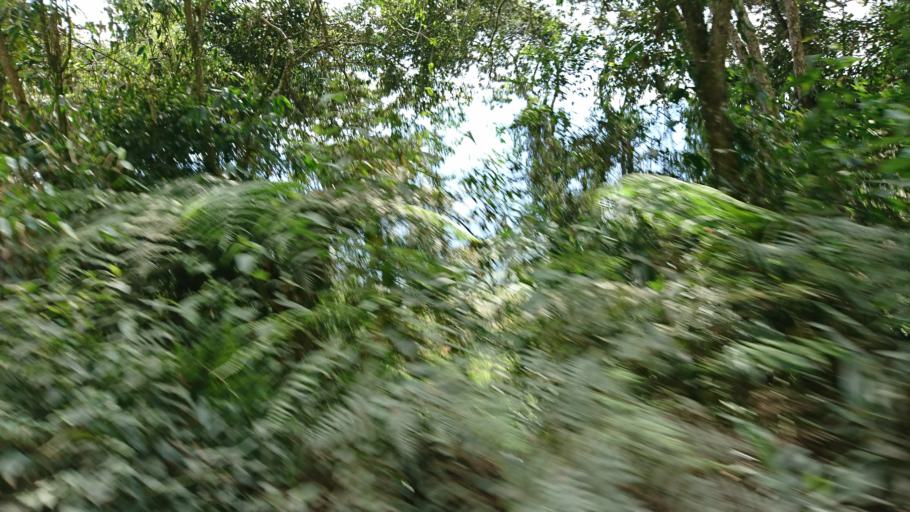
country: BO
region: La Paz
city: Coroico
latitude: -16.1151
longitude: -67.7708
